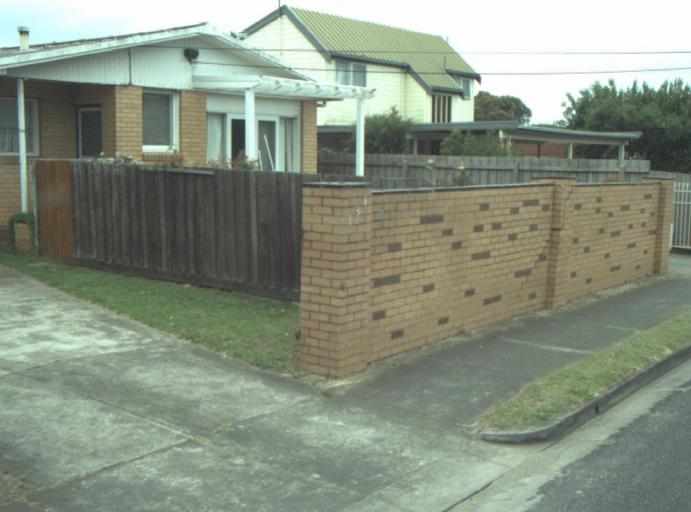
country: AU
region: Victoria
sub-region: Greater Geelong
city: Leopold
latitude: -38.2668
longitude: 144.5299
